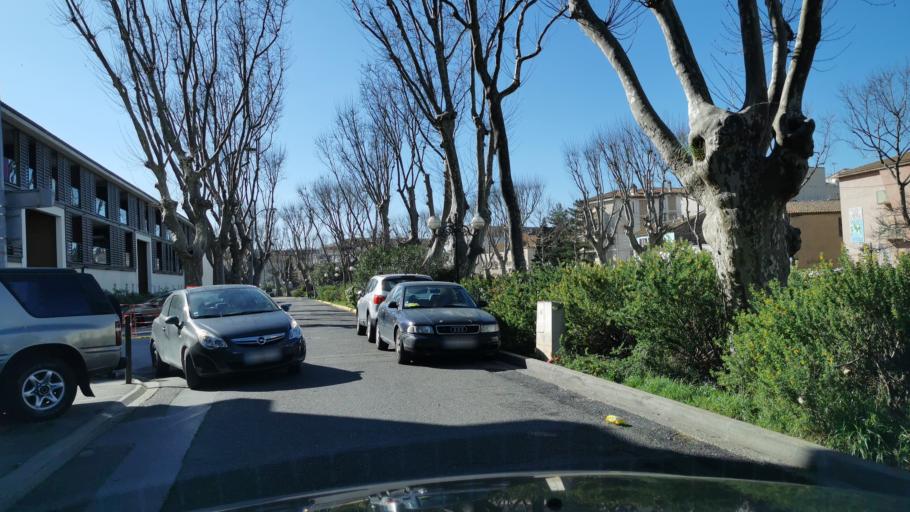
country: FR
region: Languedoc-Roussillon
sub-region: Departement de l'Aude
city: Narbonne
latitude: 43.1901
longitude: 2.9989
